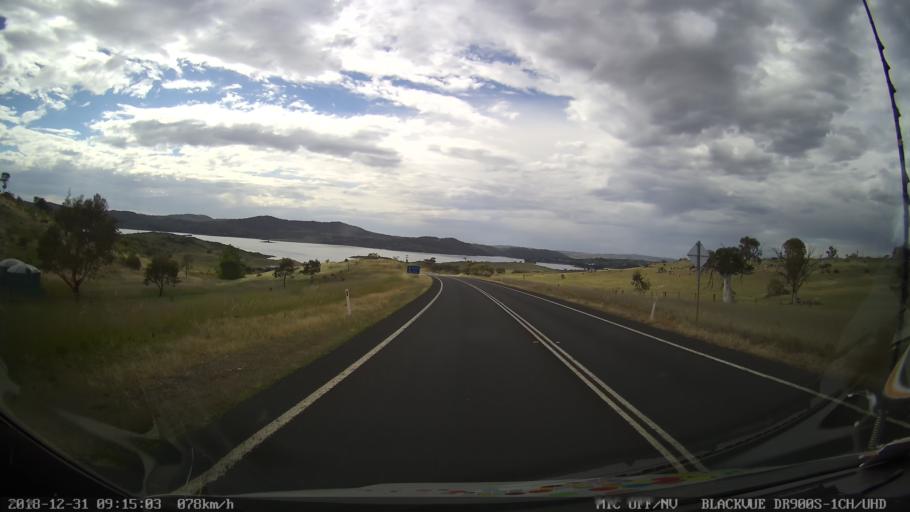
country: AU
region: New South Wales
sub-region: Snowy River
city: Jindabyne
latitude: -36.3811
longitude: 148.5963
